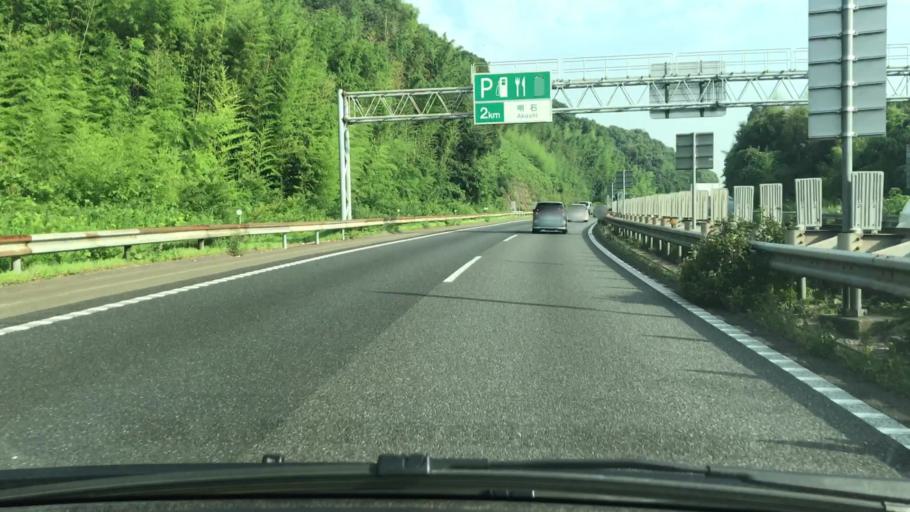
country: JP
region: Hyogo
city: Akashi
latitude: 34.6905
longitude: 134.9705
